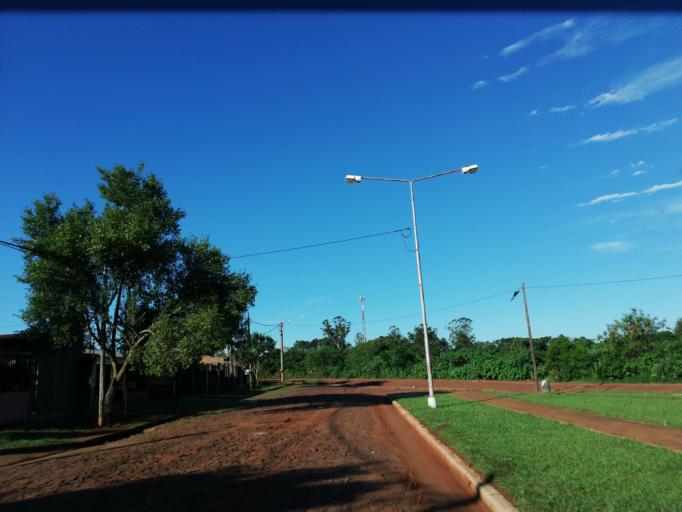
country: AR
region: Misiones
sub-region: Departamento de Capital
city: Posadas
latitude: -27.4362
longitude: -55.9358
